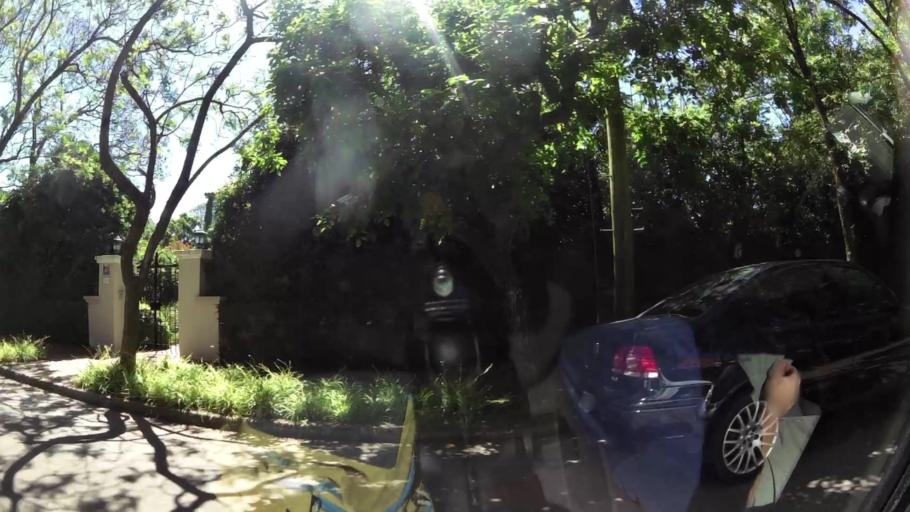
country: AR
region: Buenos Aires
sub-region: Partido de San Isidro
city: San Isidro
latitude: -34.4753
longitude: -58.4983
